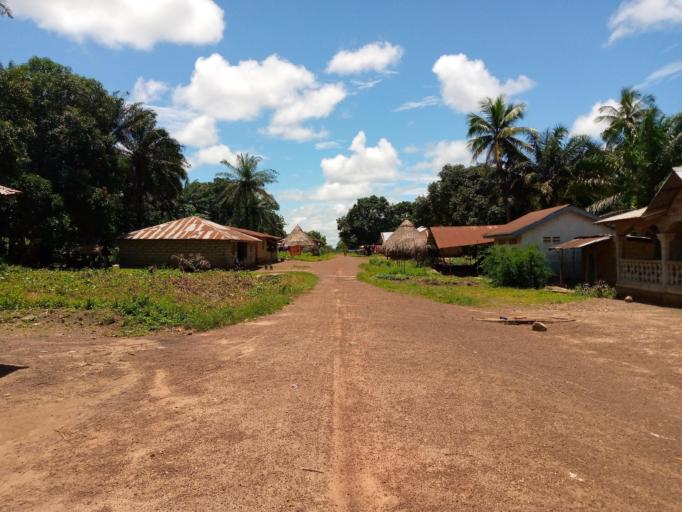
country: SL
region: Northern Province
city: Binkolo
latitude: 9.0767
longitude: -12.1448
